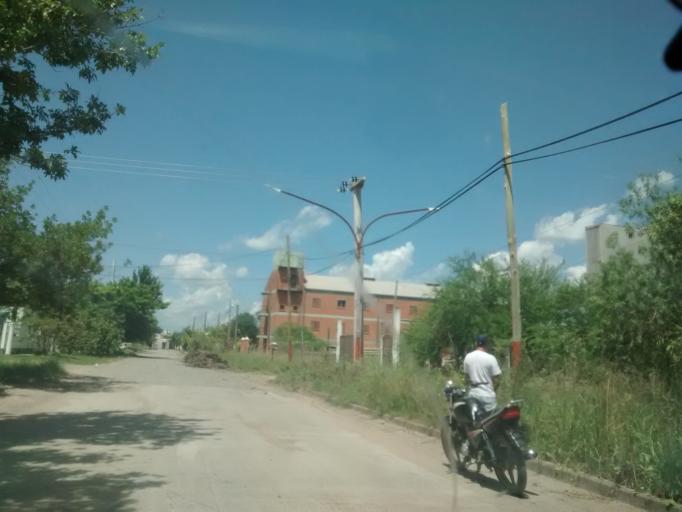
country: AR
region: Chaco
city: Resistencia
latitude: -27.4692
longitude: -58.9817
